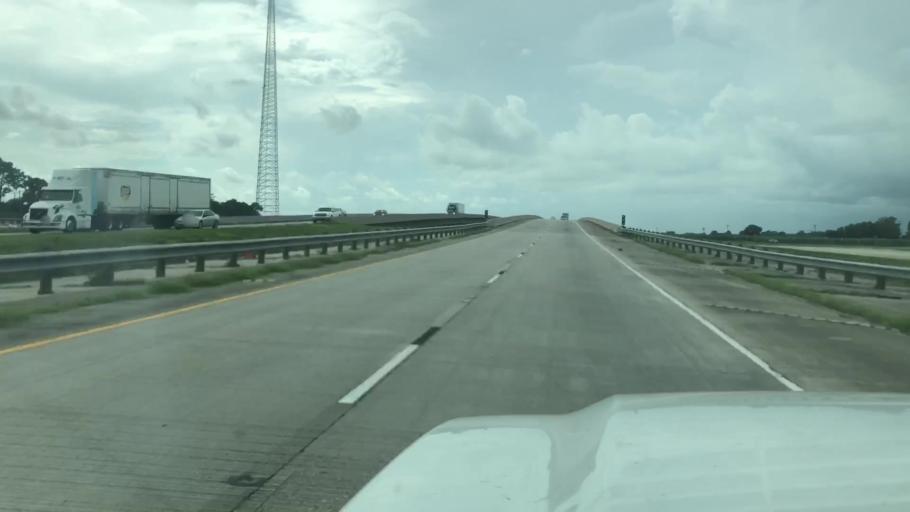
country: US
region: Louisiana
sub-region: Iberia Parish
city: Jeanerette
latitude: 29.9180
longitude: -91.7258
